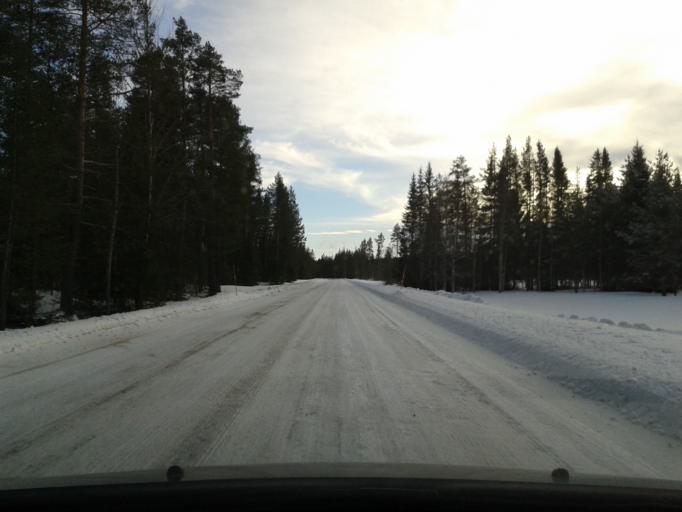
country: SE
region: Vaesterbotten
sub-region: Asele Kommun
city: Asele
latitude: 64.2558
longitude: 17.2716
